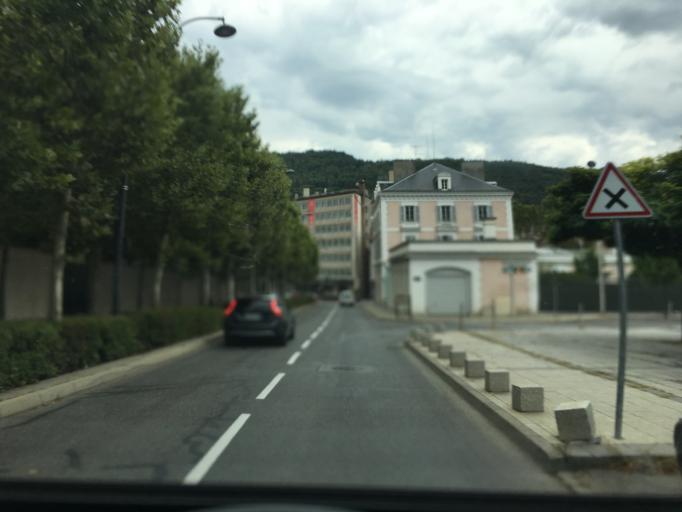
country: FR
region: Provence-Alpes-Cote d'Azur
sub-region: Departement des Hautes-Alpes
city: Gap
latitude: 44.5570
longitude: 6.0756
